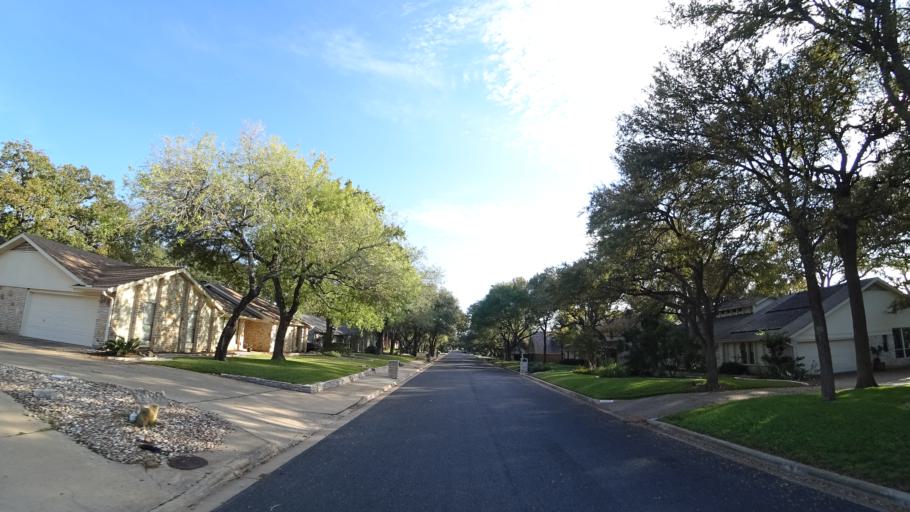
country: US
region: Texas
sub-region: Williamson County
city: Anderson Mill
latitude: 30.4363
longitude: -97.8076
